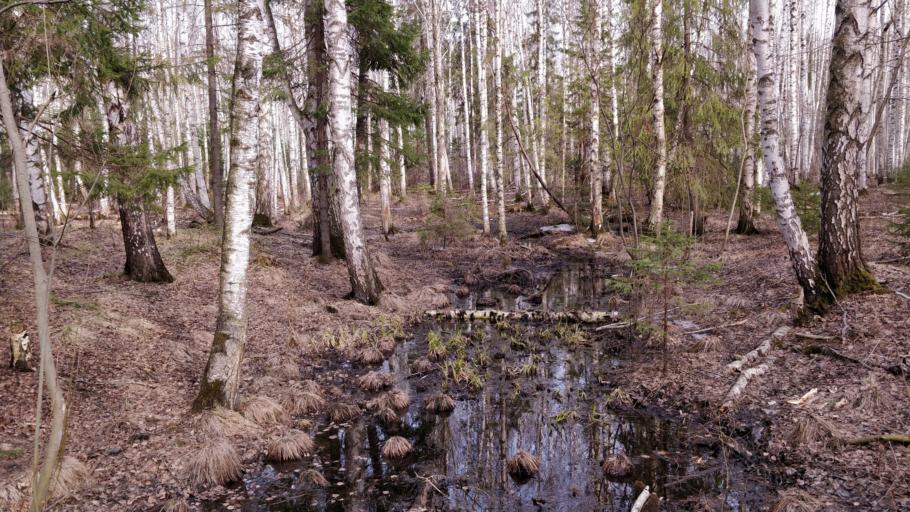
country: RU
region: Perm
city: Kondratovo
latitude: 57.9885
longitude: 56.1595
